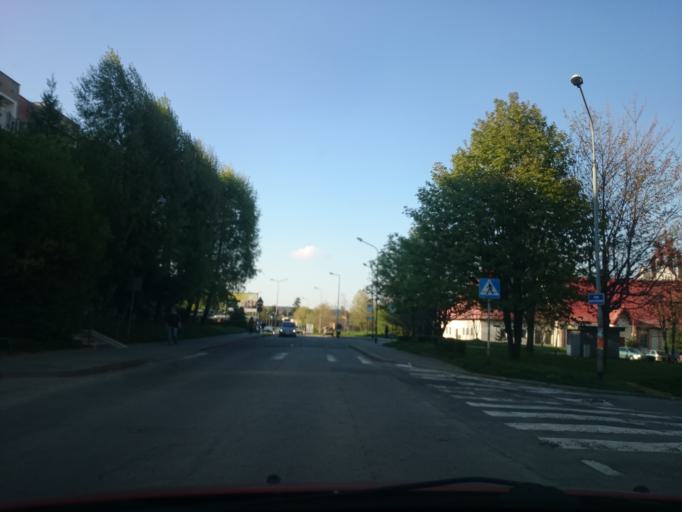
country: PL
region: Lower Silesian Voivodeship
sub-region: Powiat klodzki
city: Klodzko
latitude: 50.4367
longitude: 16.6413
